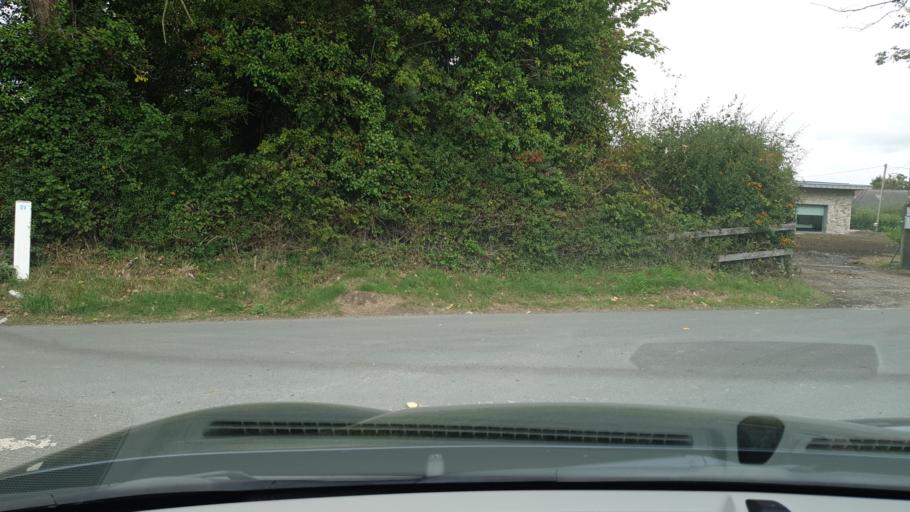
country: IE
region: Leinster
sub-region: Kildare
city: Clane
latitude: 53.2989
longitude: -6.7136
